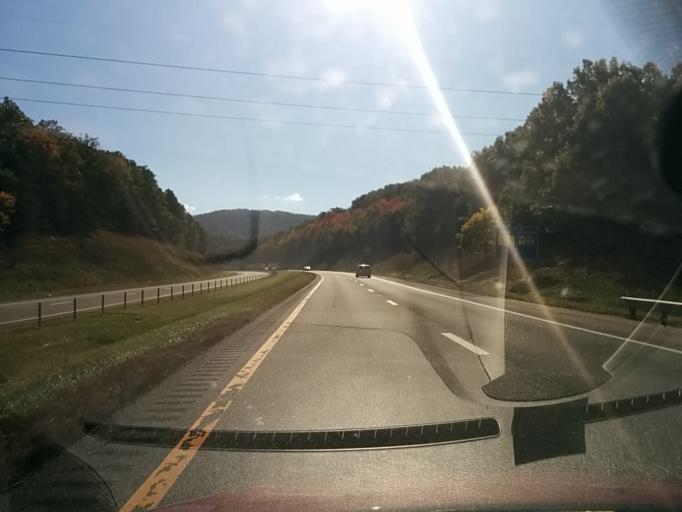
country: US
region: Virginia
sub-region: City of Waynesboro
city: Waynesboro
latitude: 38.0416
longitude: -78.8977
